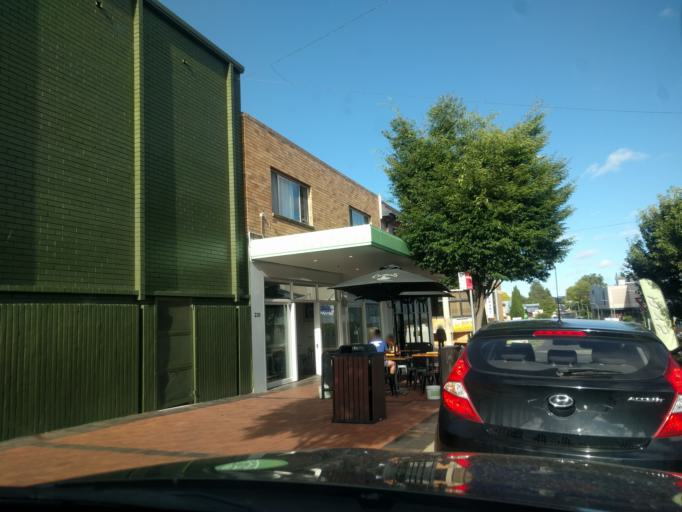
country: AU
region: New South Wales
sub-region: Armidale Dumaresq
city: Armidale
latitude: -30.5128
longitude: 151.6640
